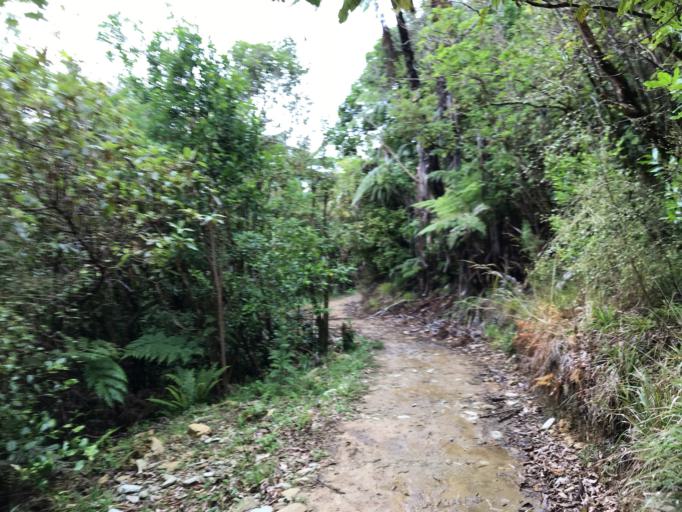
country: NZ
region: Marlborough
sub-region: Marlborough District
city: Picton
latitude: -41.1077
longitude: 174.1450
